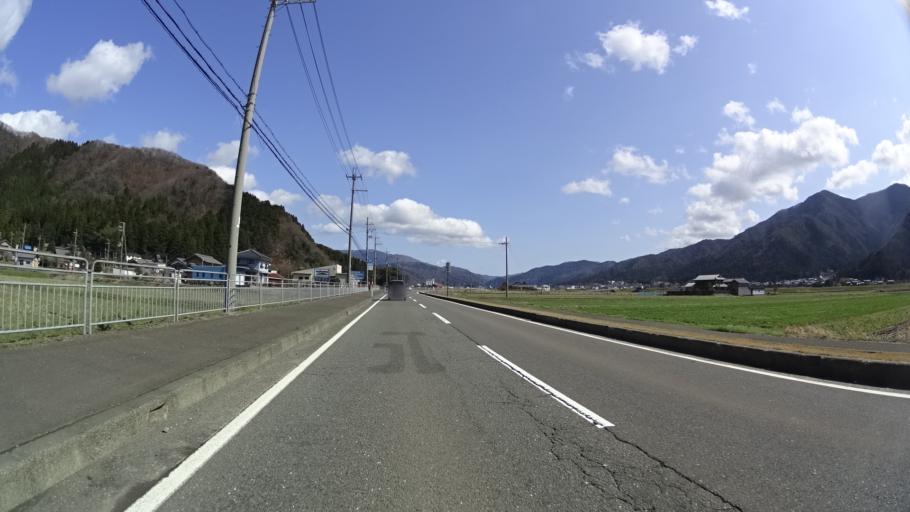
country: JP
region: Fukui
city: Obama
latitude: 35.4723
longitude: 135.8399
